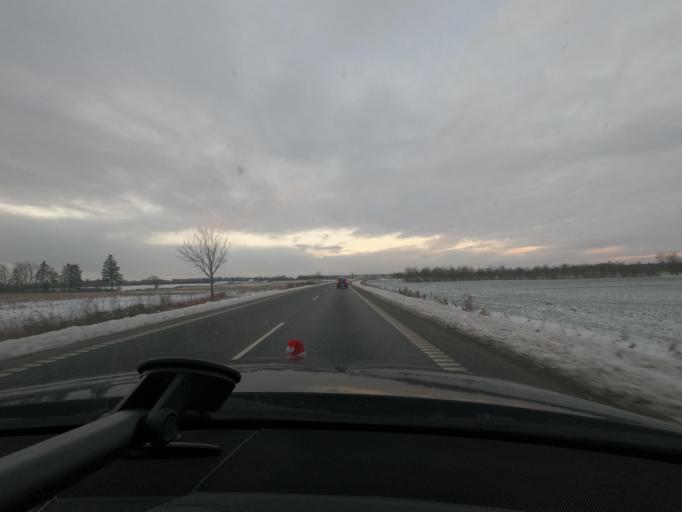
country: DK
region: South Denmark
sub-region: Aabenraa Kommune
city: Krusa
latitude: 54.8536
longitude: 9.4264
